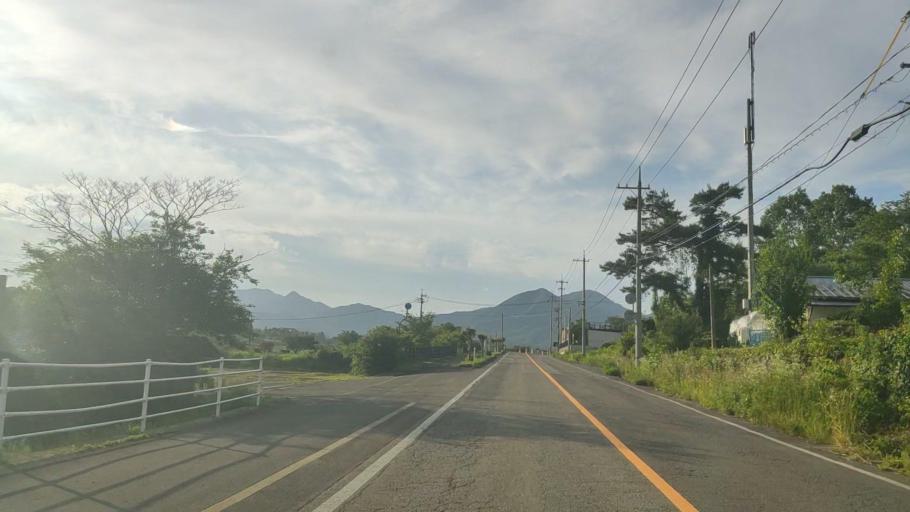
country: JP
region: Tottori
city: Kurayoshi
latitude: 35.2880
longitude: 133.6372
